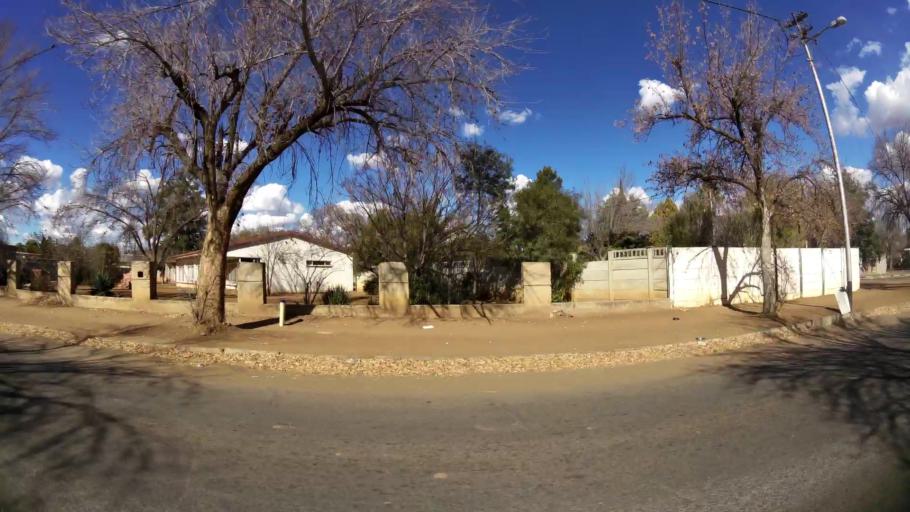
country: ZA
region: North-West
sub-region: Dr Kenneth Kaunda District Municipality
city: Klerksdorp
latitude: -26.8643
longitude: 26.6348
